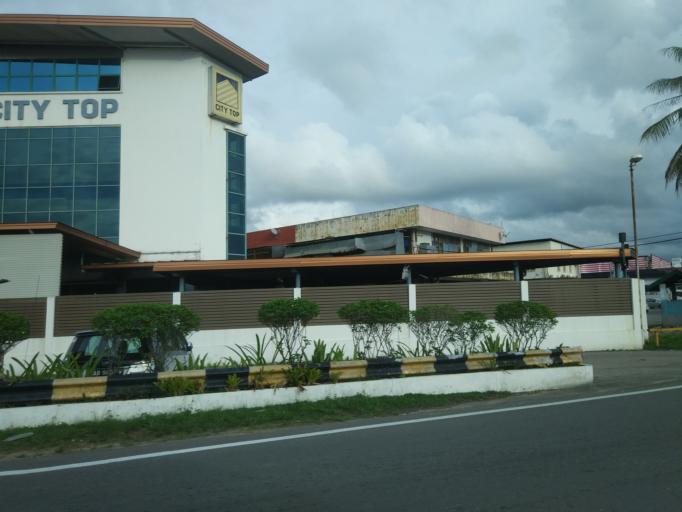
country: MY
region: Sabah
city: Kota Kinabalu
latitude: 5.9951
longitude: 116.1203
